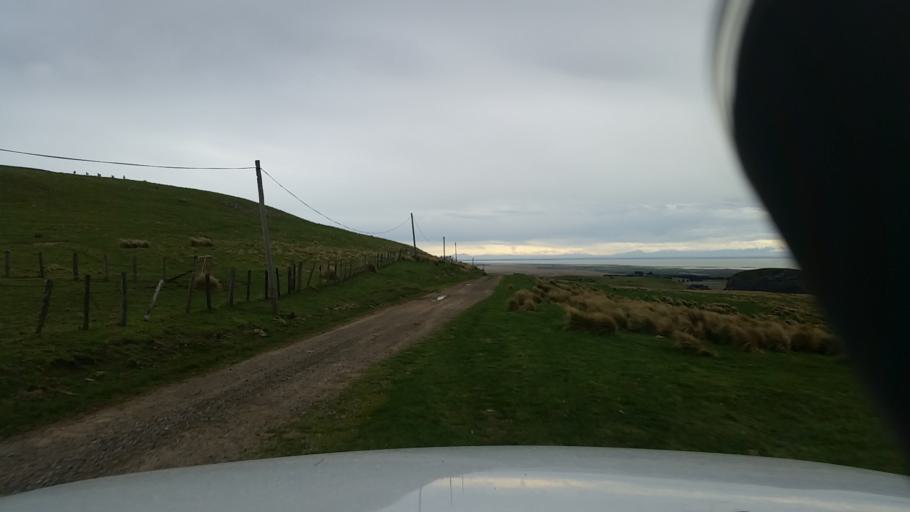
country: NZ
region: Canterbury
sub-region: Selwyn District
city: Lincoln
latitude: -43.8209
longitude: 172.7286
